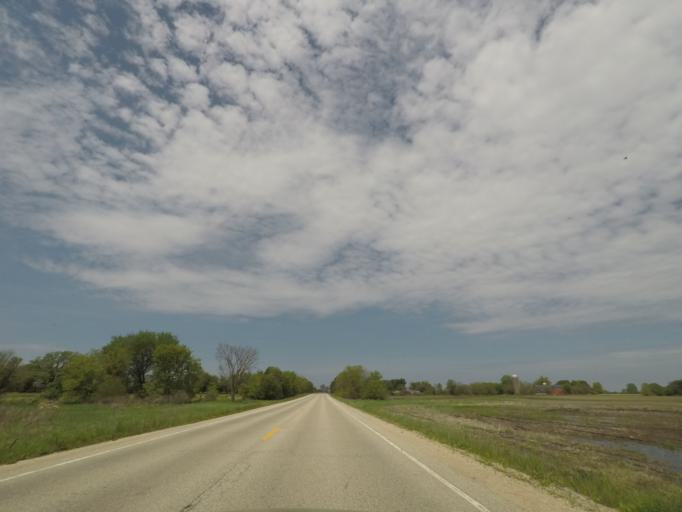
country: US
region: Wisconsin
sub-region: Rock County
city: Evansville
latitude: 42.7331
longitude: -89.2921
